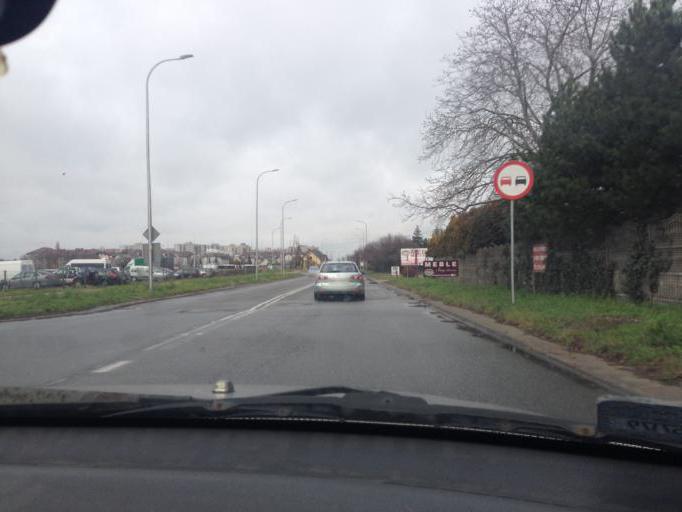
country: PL
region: Opole Voivodeship
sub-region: Powiat opolski
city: Opole
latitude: 50.6766
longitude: 17.9594
